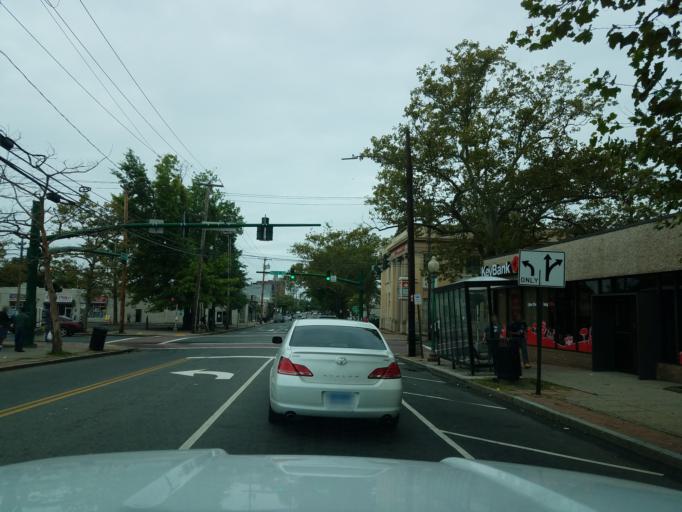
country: US
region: Connecticut
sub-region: New Haven County
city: New Haven
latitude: 41.3091
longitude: -72.8950
